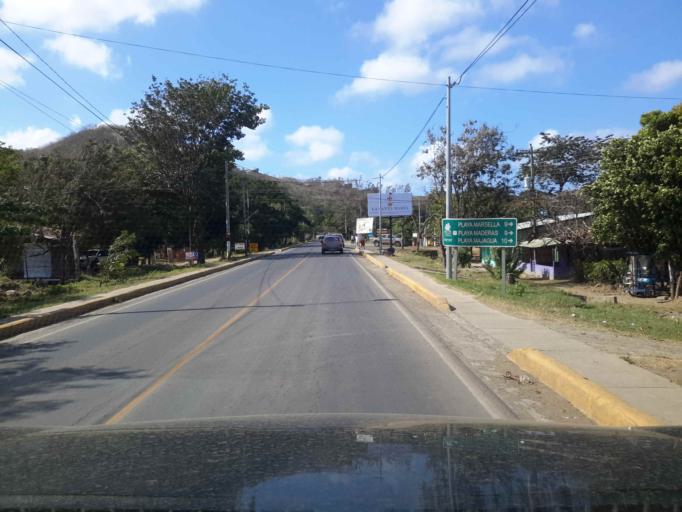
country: NI
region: Rivas
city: San Juan del Sur
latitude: 11.2598
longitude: -85.8624
